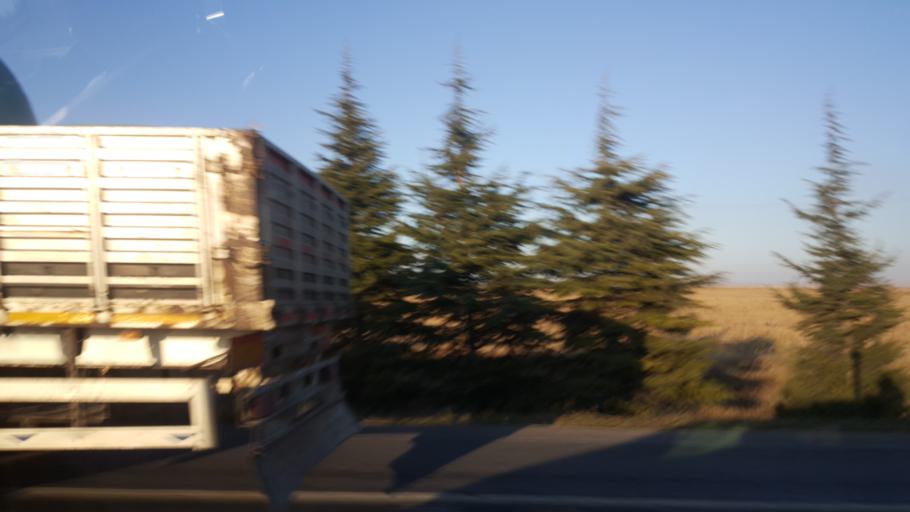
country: TR
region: Eskisehir
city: Mahmudiye
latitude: 39.5835
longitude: 30.9039
